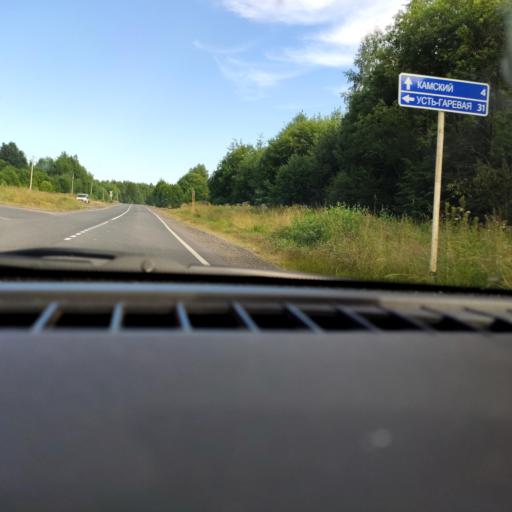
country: RU
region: Perm
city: Polazna
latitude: 58.3384
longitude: 56.1773
